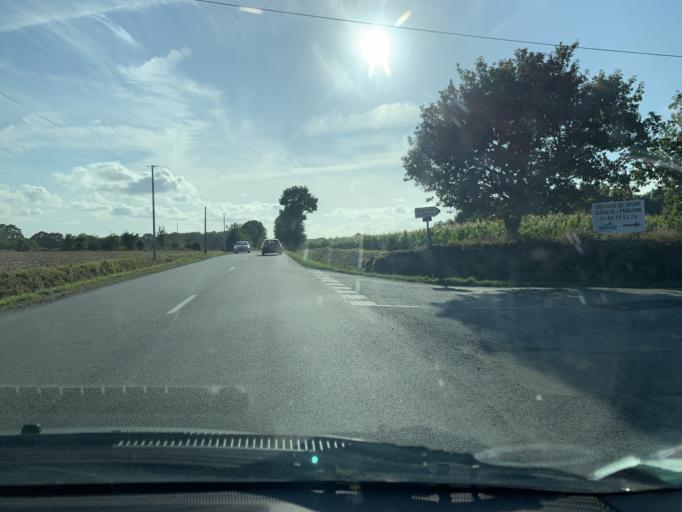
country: FR
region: Brittany
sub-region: Departement du Morbihan
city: Surzur
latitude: 47.5671
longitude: -2.6678
